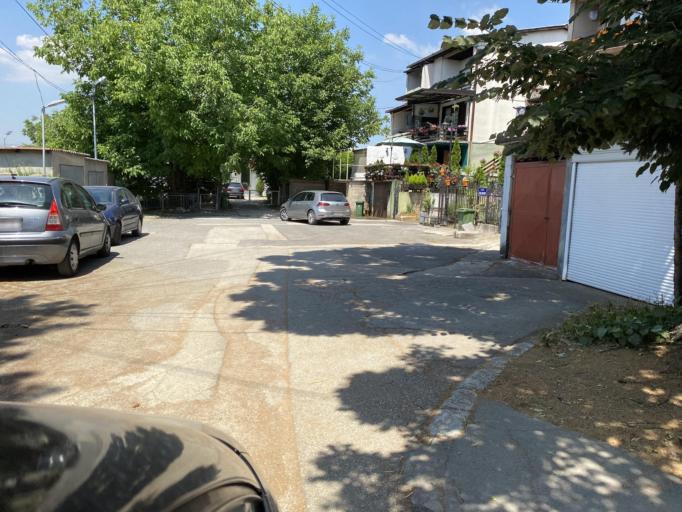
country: MK
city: Radishani
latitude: 42.0588
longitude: 21.4460
